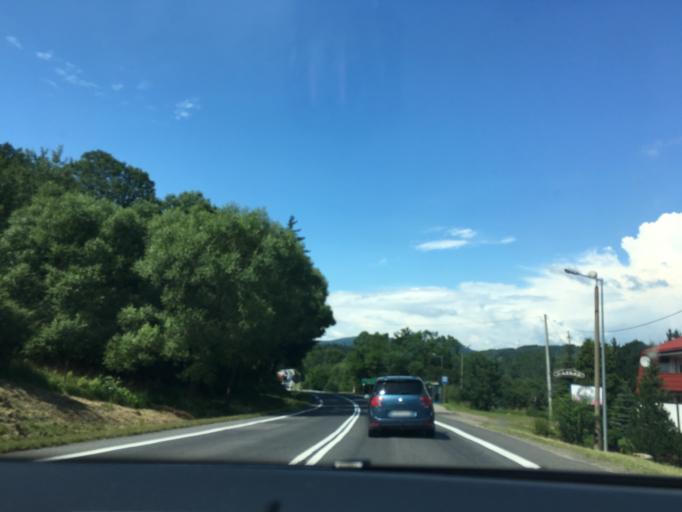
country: PL
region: Subcarpathian Voivodeship
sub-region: Powiat krosnienski
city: Dukla
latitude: 49.4740
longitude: 21.7084
